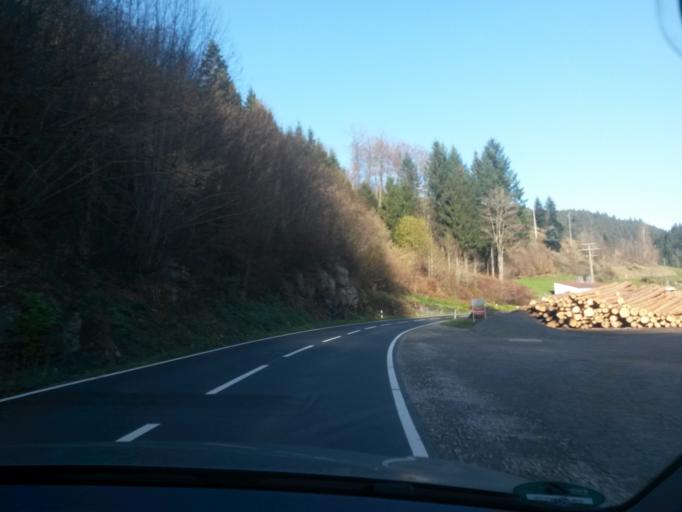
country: DE
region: Baden-Wuerttemberg
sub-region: Karlsruhe Region
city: Bad Rippoldsau-Schapbach
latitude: 48.3699
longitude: 8.2803
